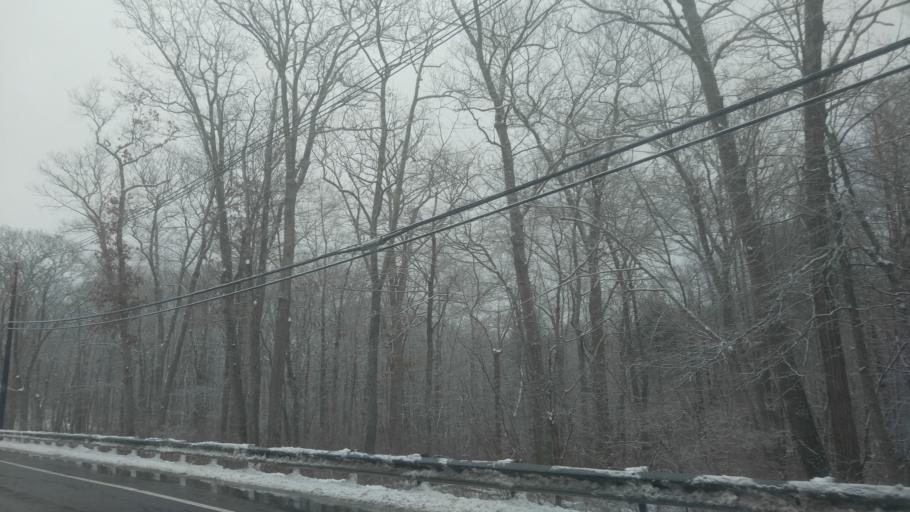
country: US
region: Rhode Island
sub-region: Providence County
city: Foster
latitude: 41.8181
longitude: -71.7161
